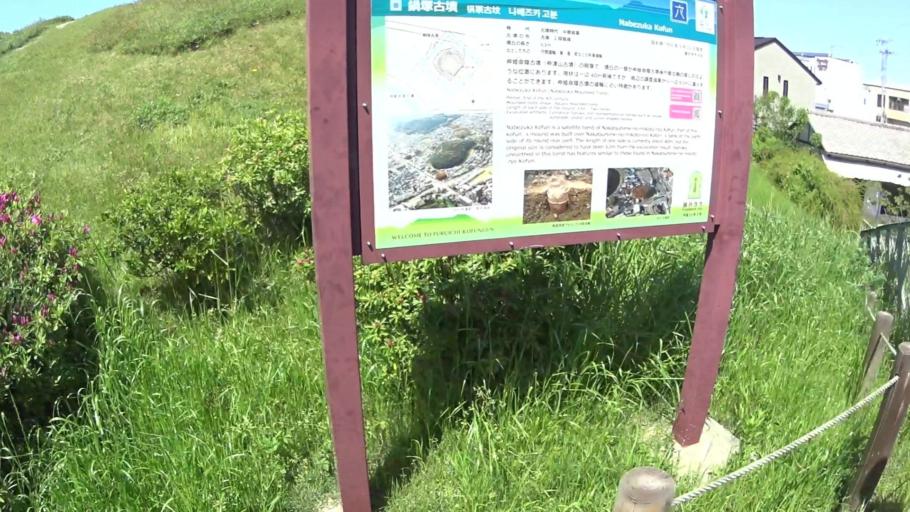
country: JP
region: Osaka
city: Kashihara
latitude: 34.5716
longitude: 135.6147
